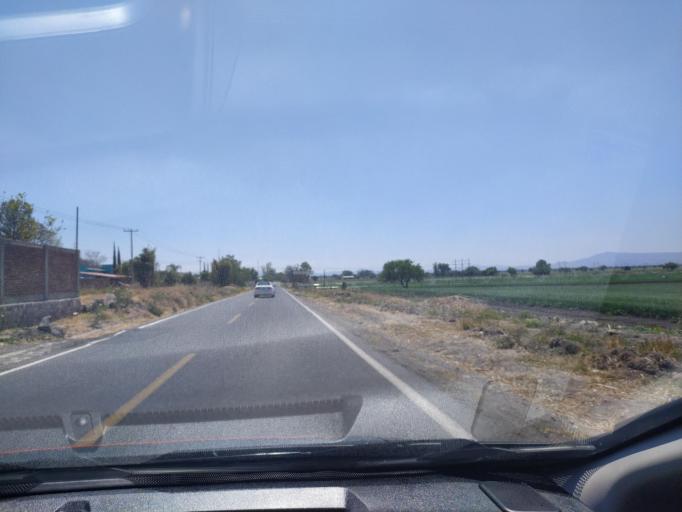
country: MX
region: Guanajuato
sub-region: San Francisco del Rincon
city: San Ignacio de Hidalgo
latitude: 20.8649
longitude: -101.8605
